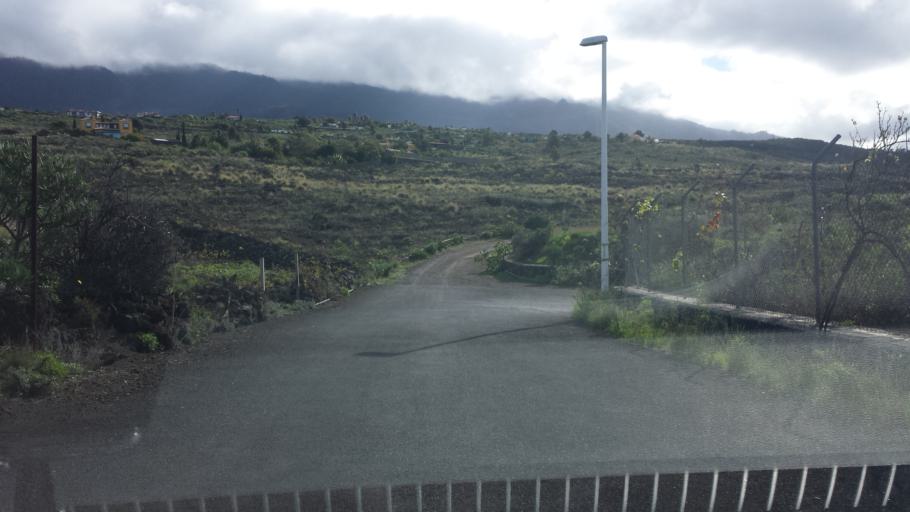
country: ES
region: Canary Islands
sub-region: Provincia de Santa Cruz de Tenerife
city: El Paso
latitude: 28.6085
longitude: -17.8991
